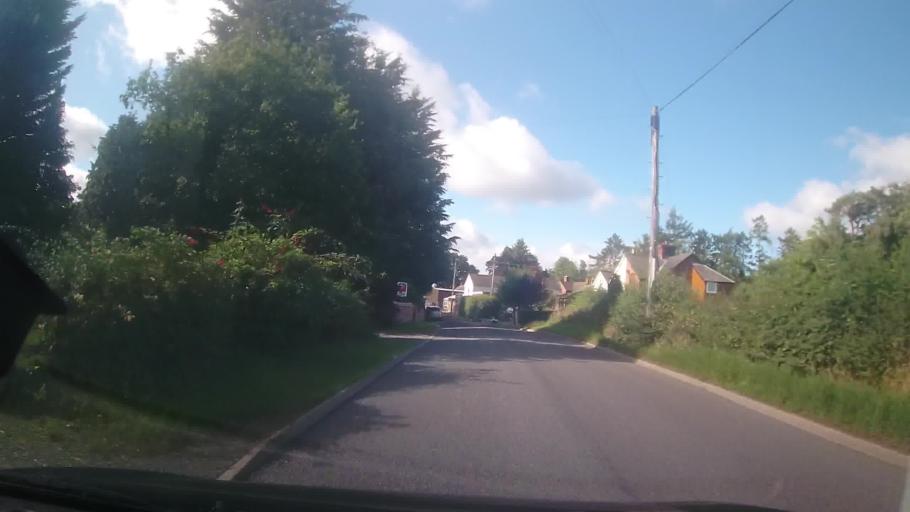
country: GB
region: England
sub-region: Shropshire
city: Bicton
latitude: 52.7545
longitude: -2.8313
